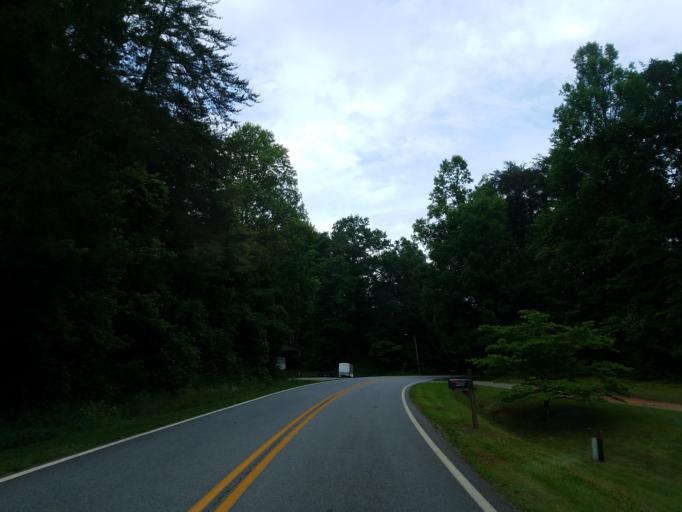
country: US
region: Georgia
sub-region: Lumpkin County
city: Dahlonega
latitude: 34.6133
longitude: -83.9757
